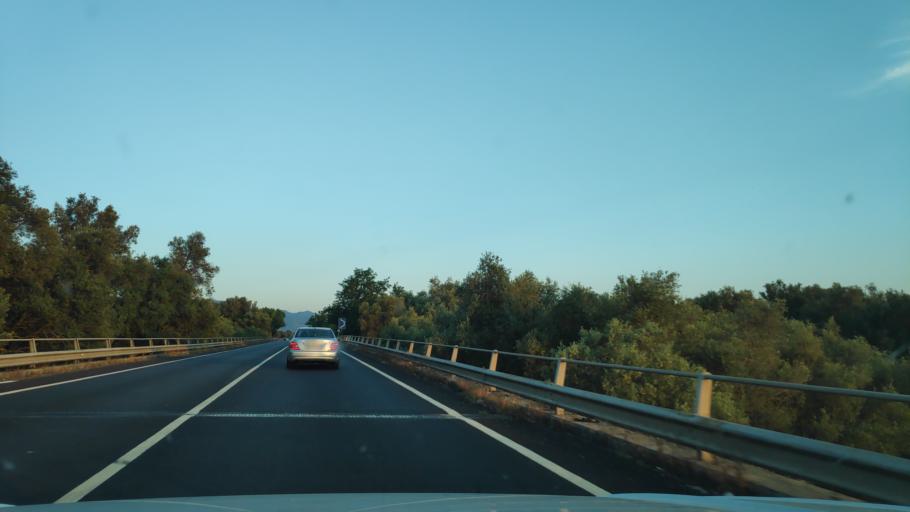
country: IT
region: Calabria
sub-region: Provincia di Reggio Calabria
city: Melicucco
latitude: 38.4358
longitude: 16.0480
